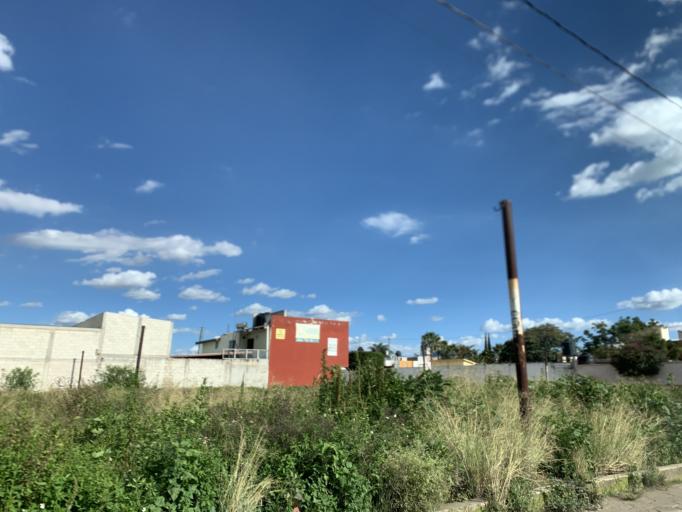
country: MX
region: Puebla
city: Cholula
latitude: 19.0548
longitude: -98.3144
